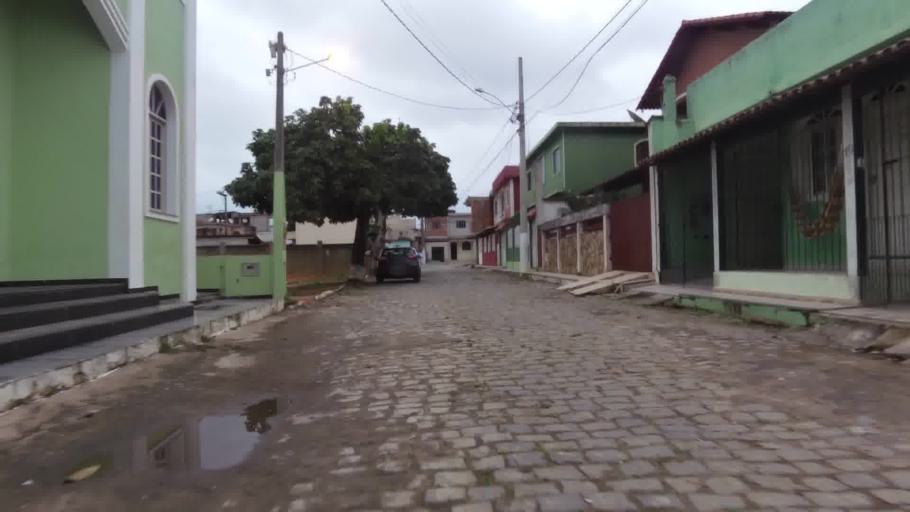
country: BR
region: Espirito Santo
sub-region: Marataizes
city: Marataizes
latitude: -21.0443
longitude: -40.8345
